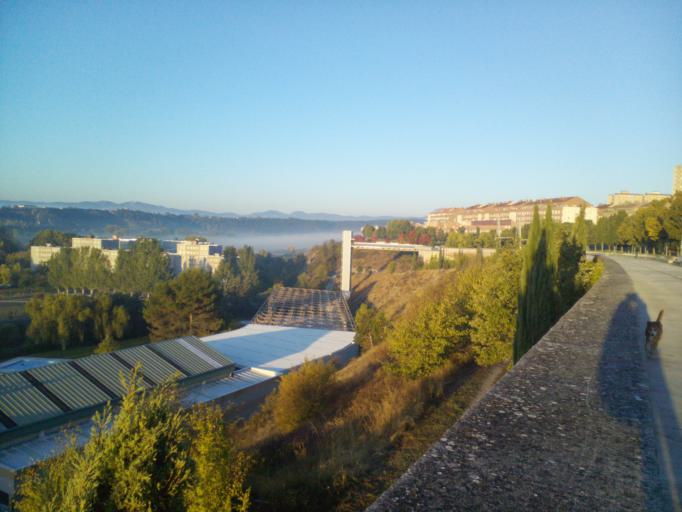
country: ES
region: Navarre
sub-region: Provincia de Navarra
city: Baranain
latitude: 42.8024
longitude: -1.6726
